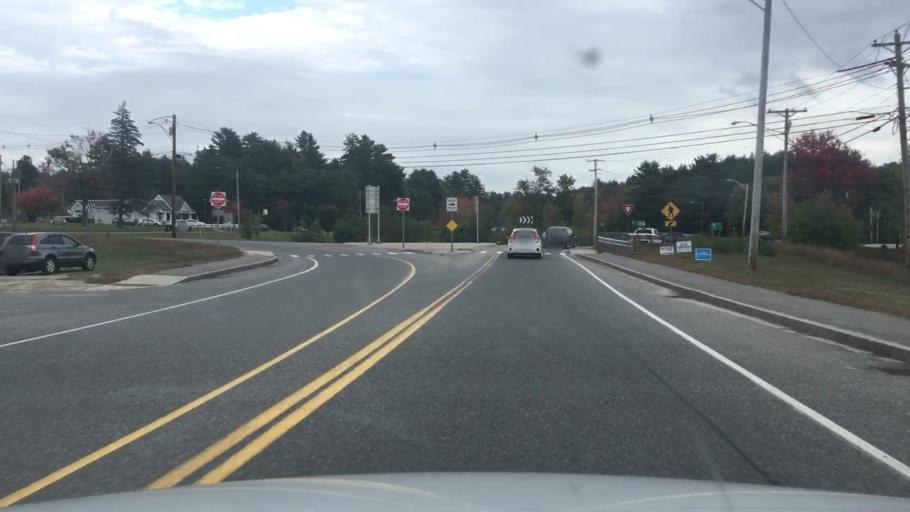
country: US
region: New Hampshire
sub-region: Strafford County
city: New Durham
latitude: 43.4520
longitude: -71.2130
